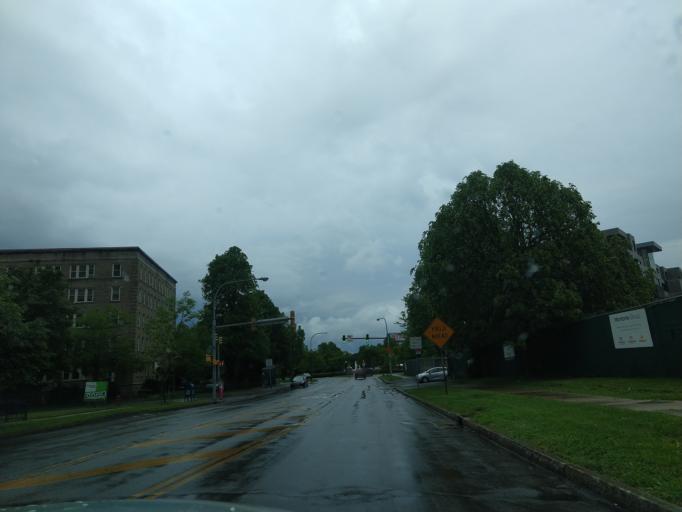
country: US
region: New York
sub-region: Erie County
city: Buffalo
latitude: 42.9190
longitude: -78.8682
